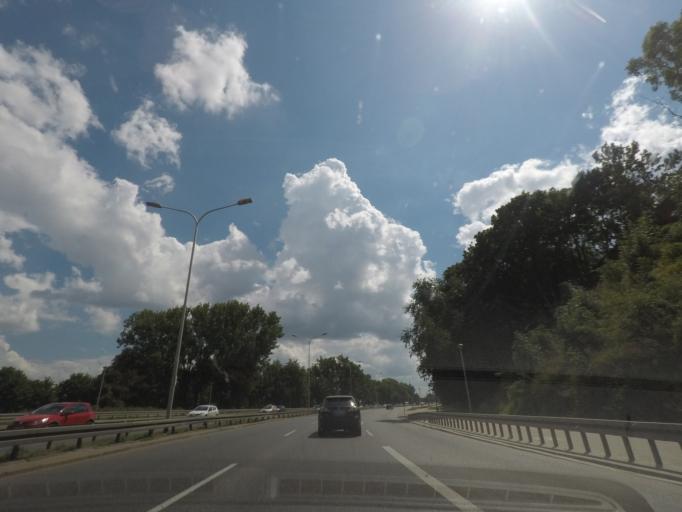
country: PL
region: Masovian Voivodeship
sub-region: Warszawa
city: Zoliborz
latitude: 52.2675
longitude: 21.0019
